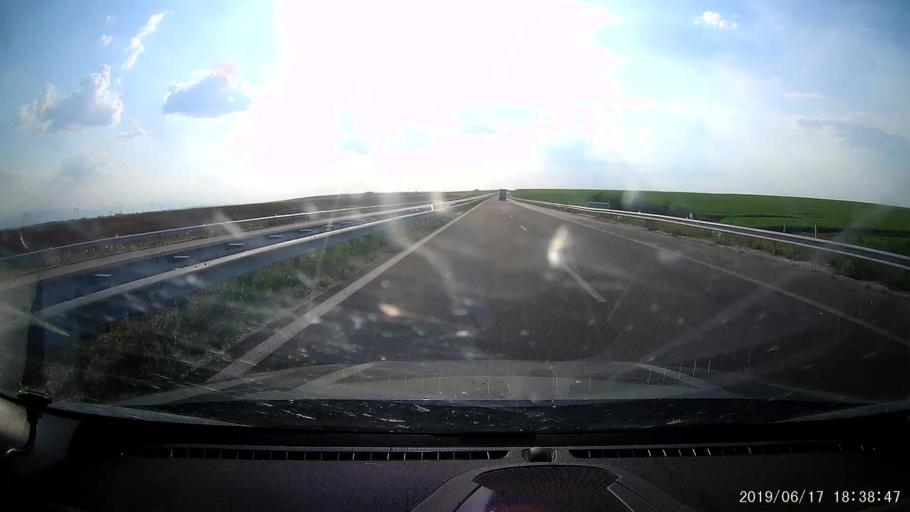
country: BG
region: Stara Zagora
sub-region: Obshtina Chirpan
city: Chirpan
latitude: 42.1393
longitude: 25.3269
